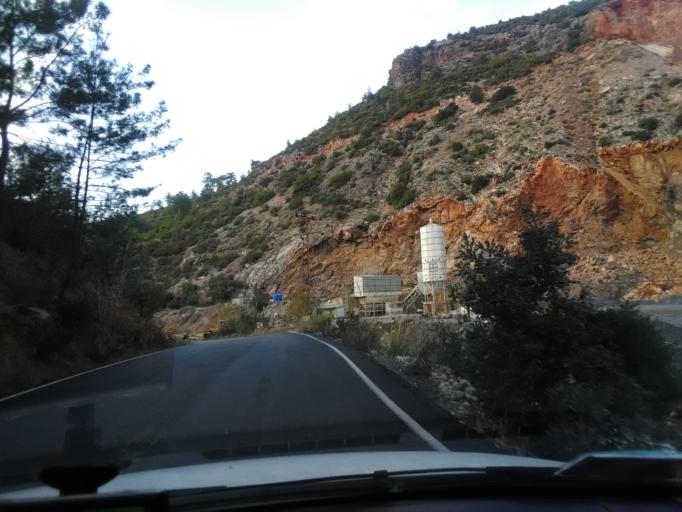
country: TR
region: Antalya
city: Gazipasa
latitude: 36.2799
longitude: 32.3626
